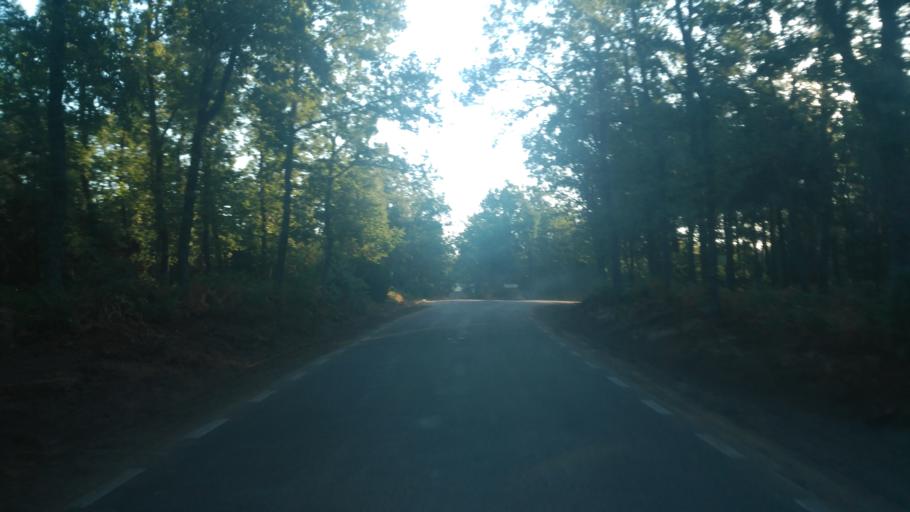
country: ES
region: Castille and Leon
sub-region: Provincia de Salamanca
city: Nava de Francia
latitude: 40.5248
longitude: -6.1350
